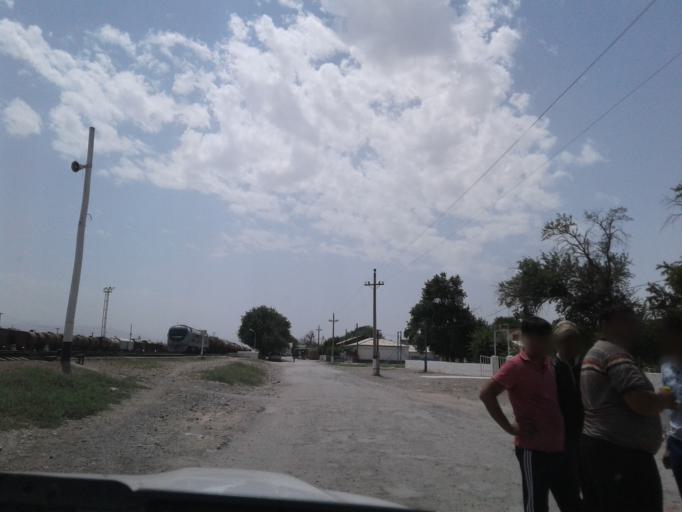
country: IR
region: Razavi Khorasan
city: Kalat-e Naderi
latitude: 37.2013
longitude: 60.0349
